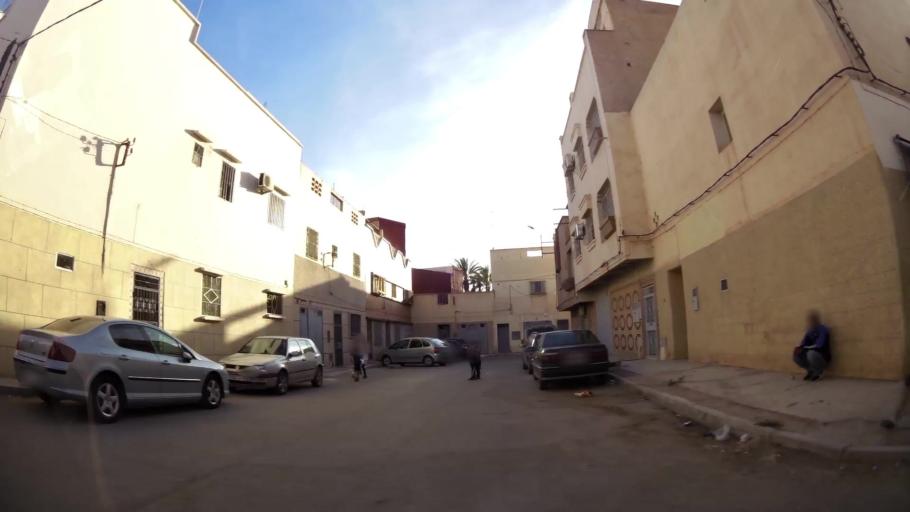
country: MA
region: Oriental
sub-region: Oujda-Angad
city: Oujda
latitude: 34.6779
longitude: -1.9045
